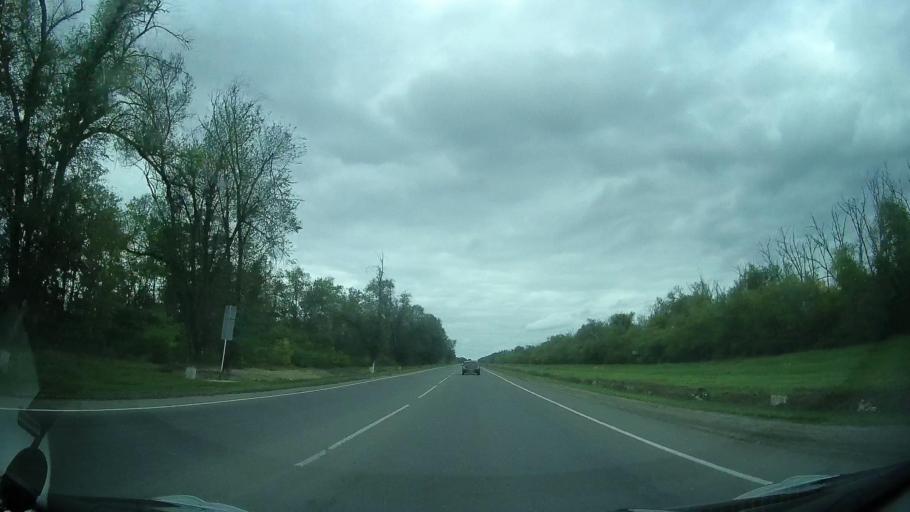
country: RU
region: Rostov
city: Yegorlykskaya
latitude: 46.5931
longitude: 40.6261
